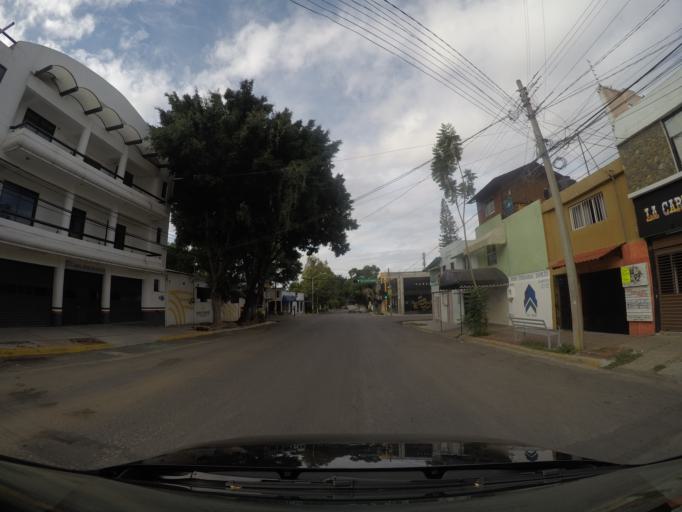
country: MX
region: Oaxaca
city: Oaxaca de Juarez
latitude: 17.0757
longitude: -96.7161
